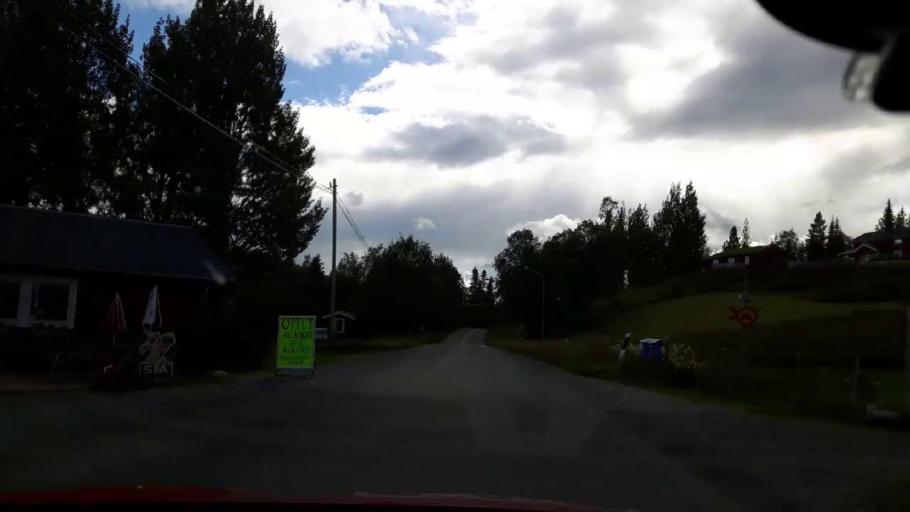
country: SE
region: Jaemtland
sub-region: Are Kommun
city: Are
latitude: 63.1659
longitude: 13.0594
